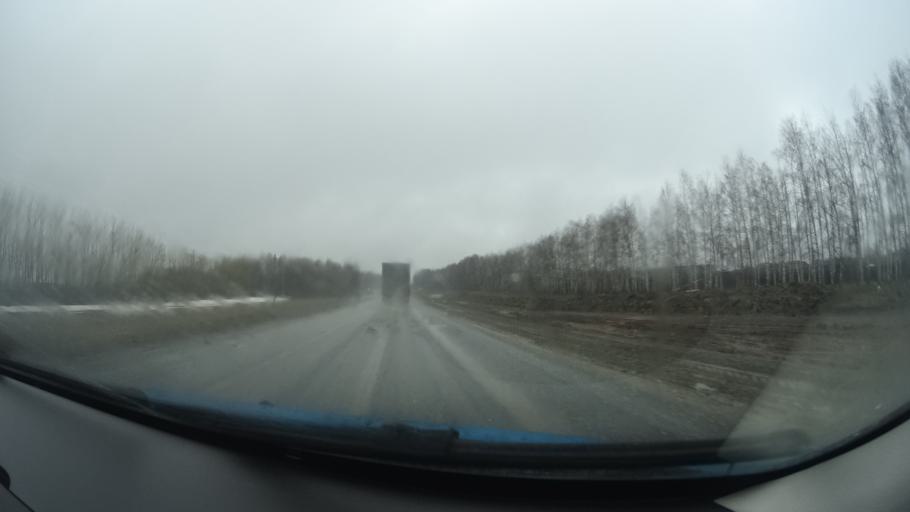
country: RU
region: Bashkortostan
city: Buzdyak
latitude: 54.6895
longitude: 54.8162
